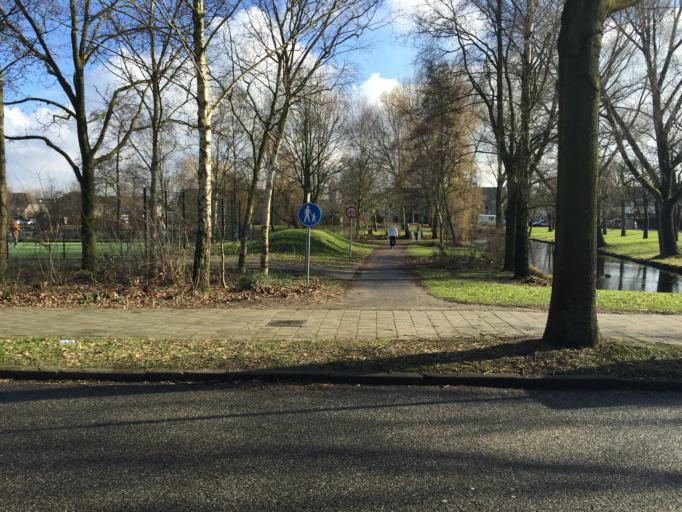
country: NL
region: Utrecht
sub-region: Gemeente Montfoort
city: Montfoort
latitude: 52.0925
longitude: 4.9552
